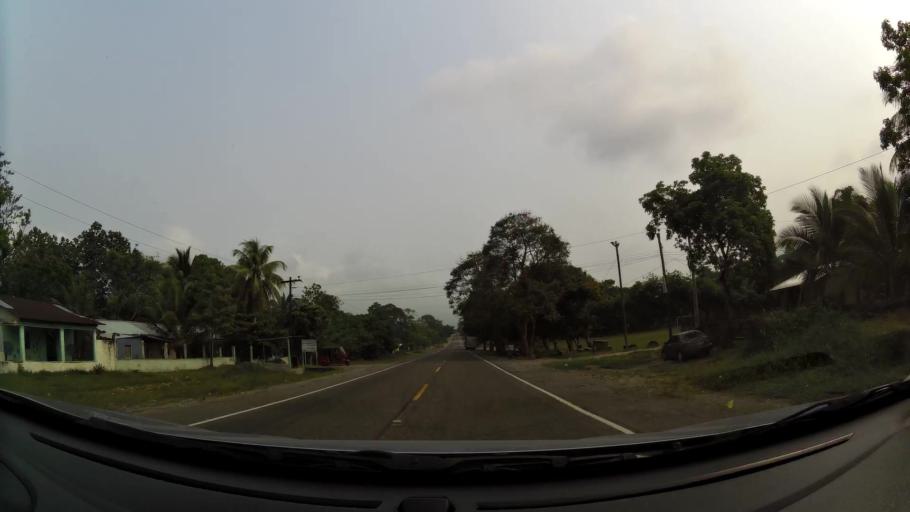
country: HN
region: Atlantida
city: Mezapa
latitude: 15.6017
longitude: -87.6104
